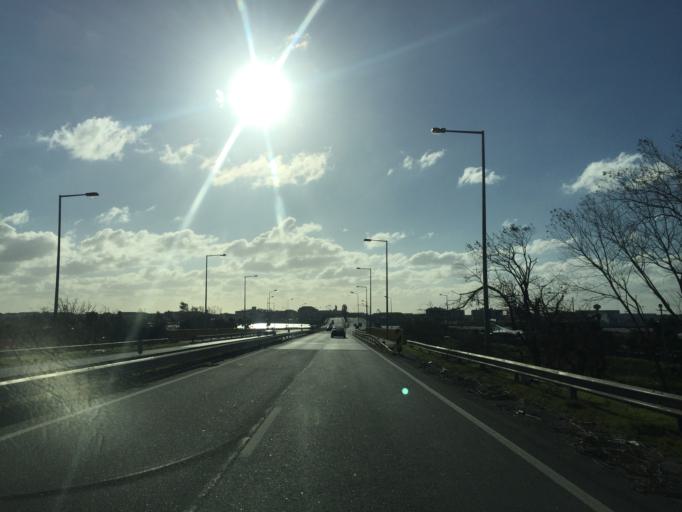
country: PT
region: Coimbra
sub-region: Figueira da Foz
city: Figueira da Foz
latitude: 40.1376
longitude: -8.8473
